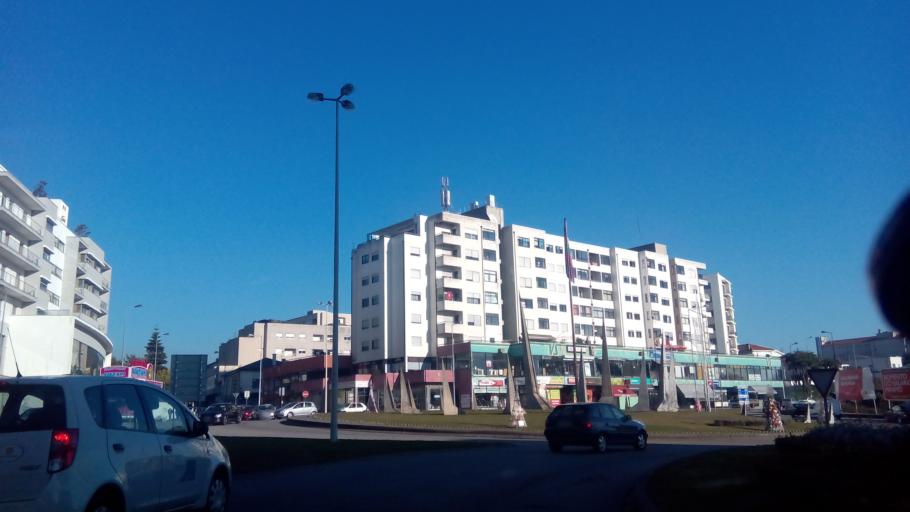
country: PT
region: Porto
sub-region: Paredes
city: Casteloes de Cepeda
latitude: 41.2062
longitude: -8.3362
